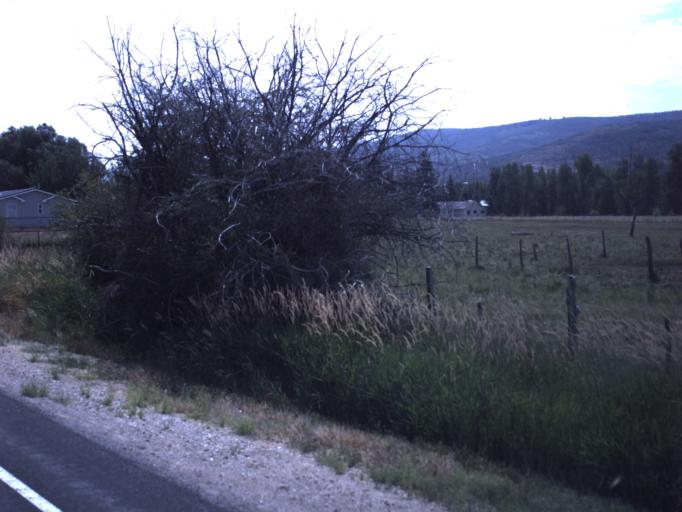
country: US
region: Utah
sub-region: Summit County
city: Francis
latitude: 40.5829
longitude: -111.2346
